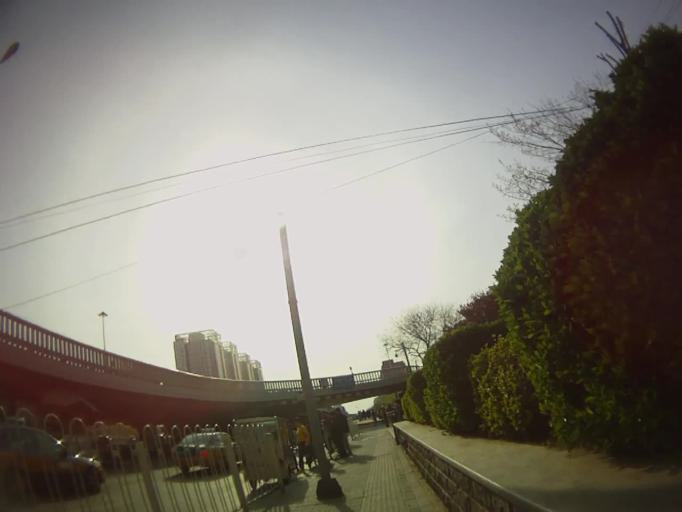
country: CN
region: Beijing
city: Longtan
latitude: 39.8926
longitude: 116.4391
